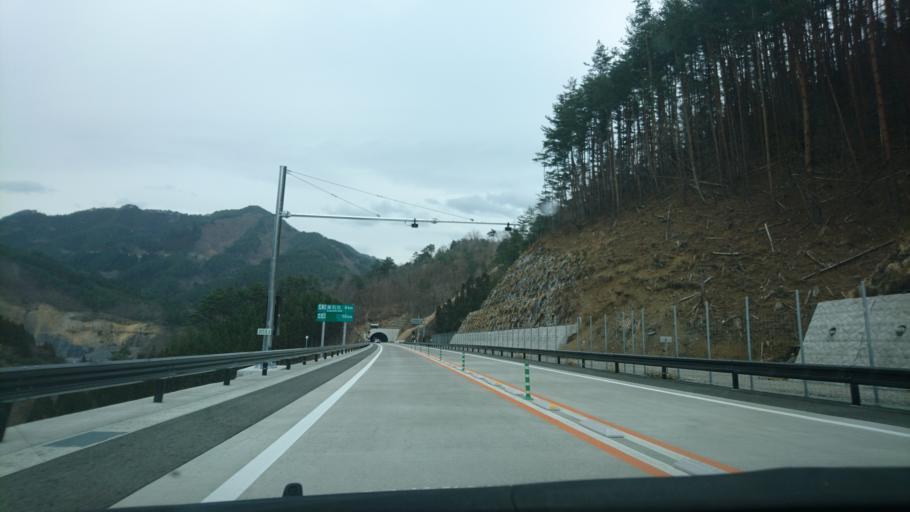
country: JP
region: Iwate
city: Kamaishi
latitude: 39.2881
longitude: 141.8633
